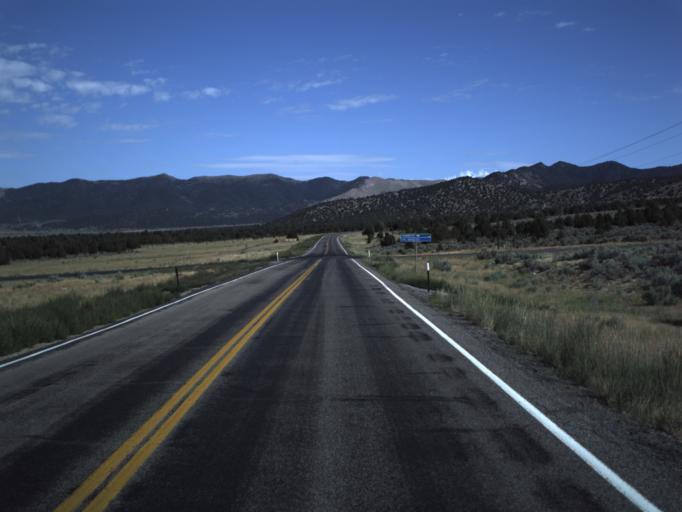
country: US
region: Utah
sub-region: Utah County
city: Genola
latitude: 39.9273
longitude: -112.1474
